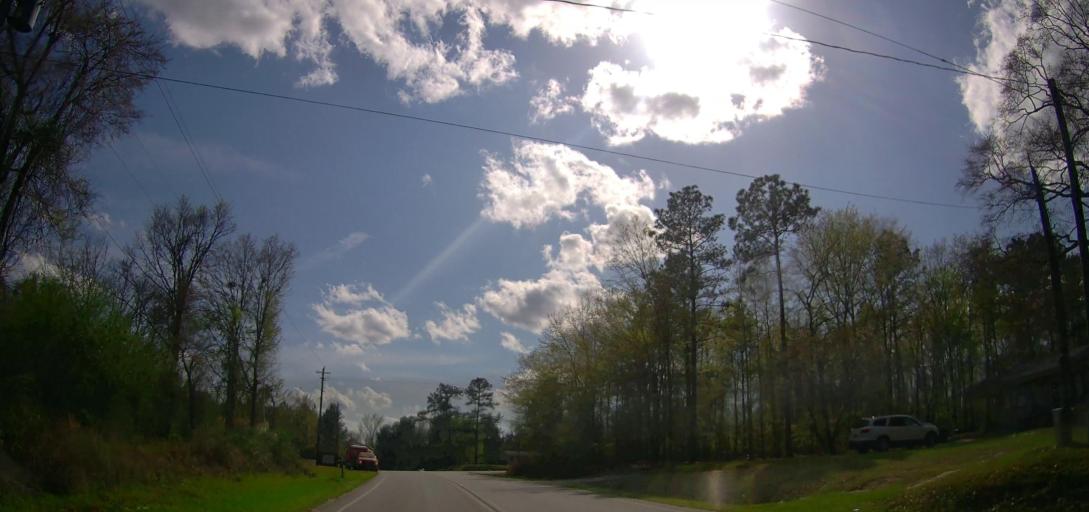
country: US
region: Georgia
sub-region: Wilkinson County
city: Gordon
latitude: 32.9668
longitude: -83.2885
